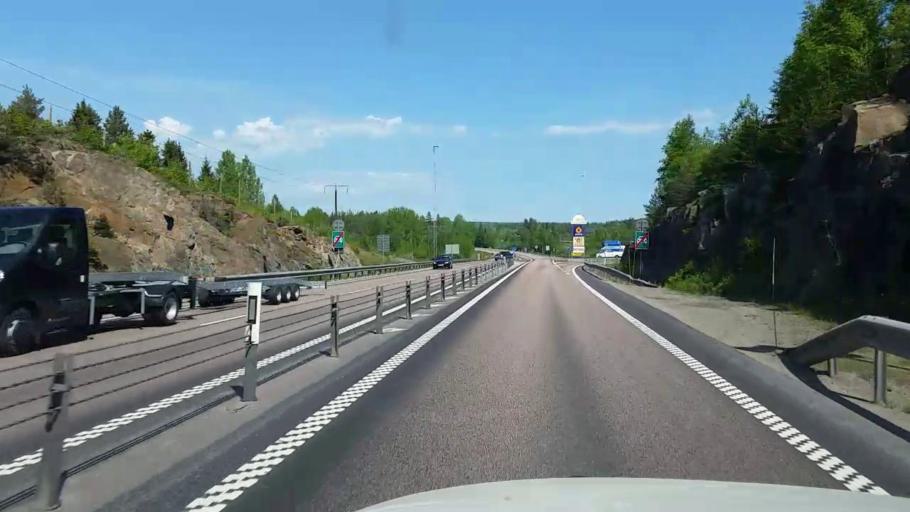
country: SE
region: Gaevleborg
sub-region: Hudiksvalls Kommun
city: Hudiksvall
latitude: 61.7412
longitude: 17.0745
